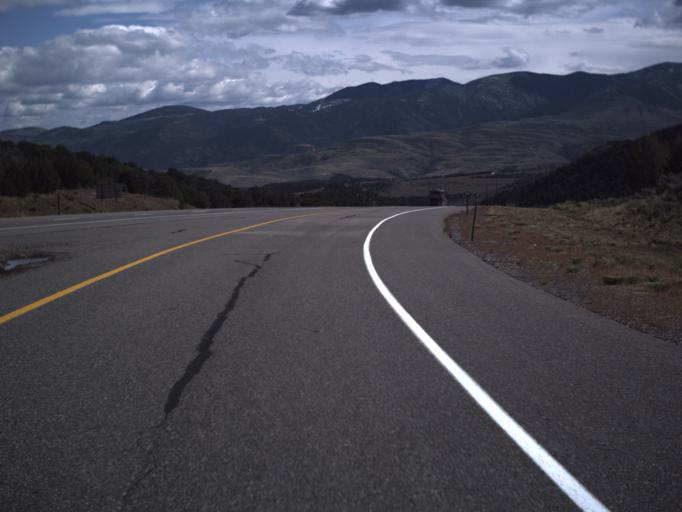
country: US
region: Utah
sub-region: Beaver County
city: Beaver
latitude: 38.5857
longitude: -112.4885
